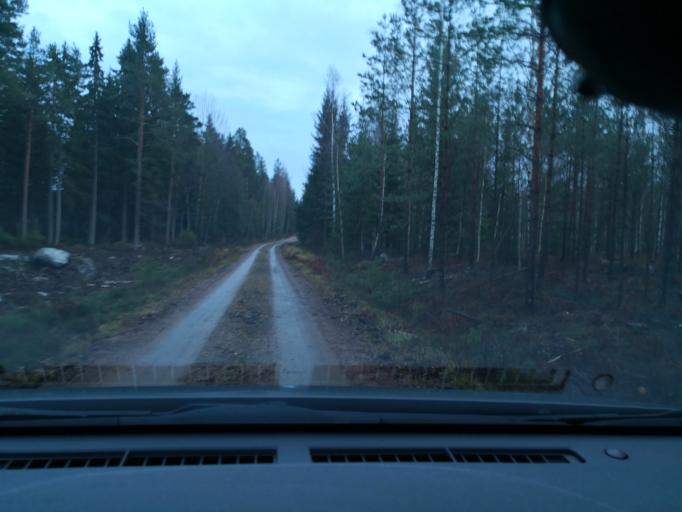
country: SE
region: Vaestmanland
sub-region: Hallstahammars Kommun
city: Hallstahammar
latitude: 59.5554
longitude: 16.1617
